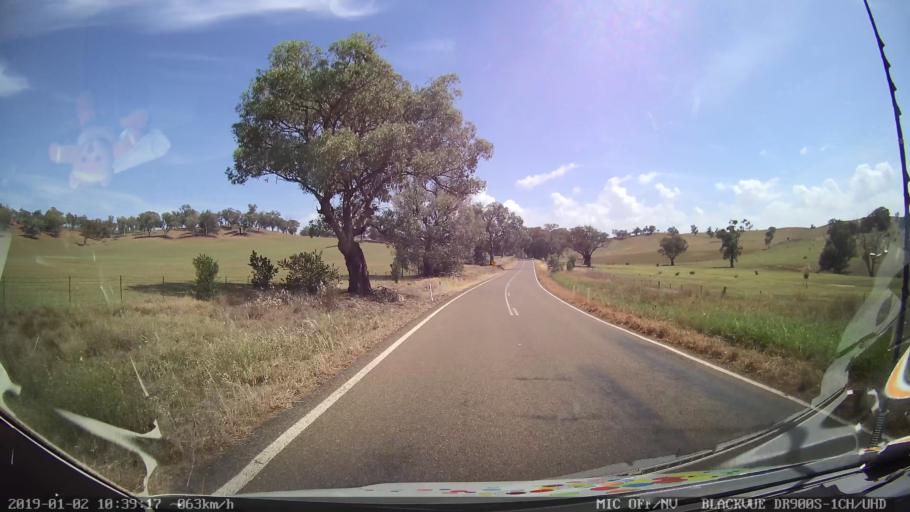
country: AU
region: New South Wales
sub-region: Gundagai
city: Gundagai
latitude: -34.8124
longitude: 148.3195
